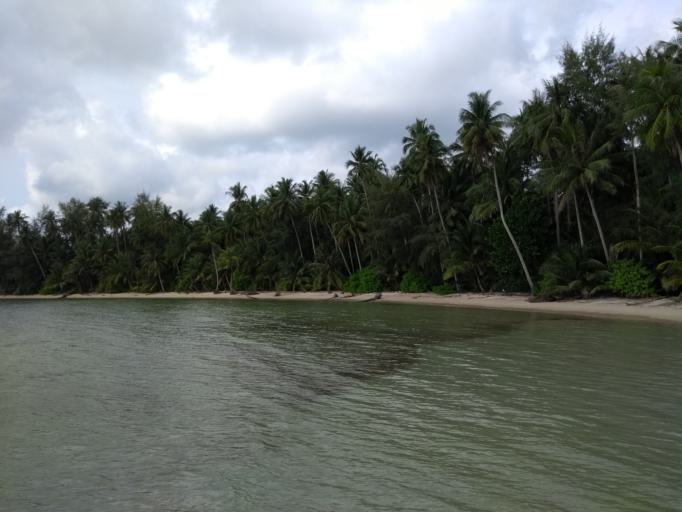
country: TH
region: Trat
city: Ko Kut
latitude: 11.6222
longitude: 102.5451
